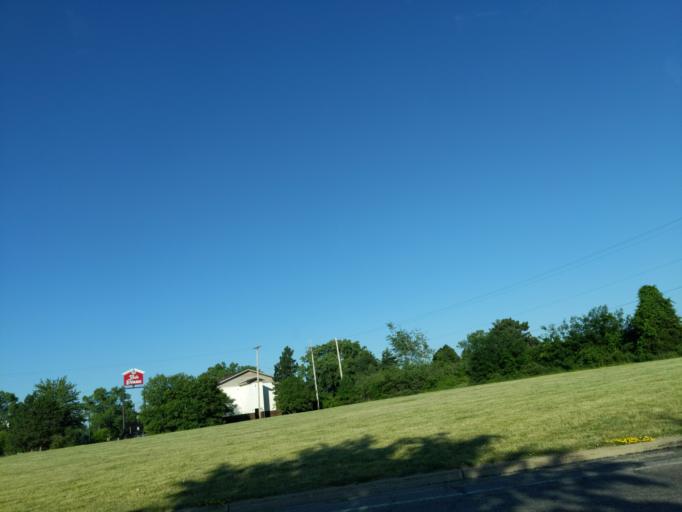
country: US
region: Michigan
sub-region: Ingham County
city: Holt
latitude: 42.6603
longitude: -84.5414
